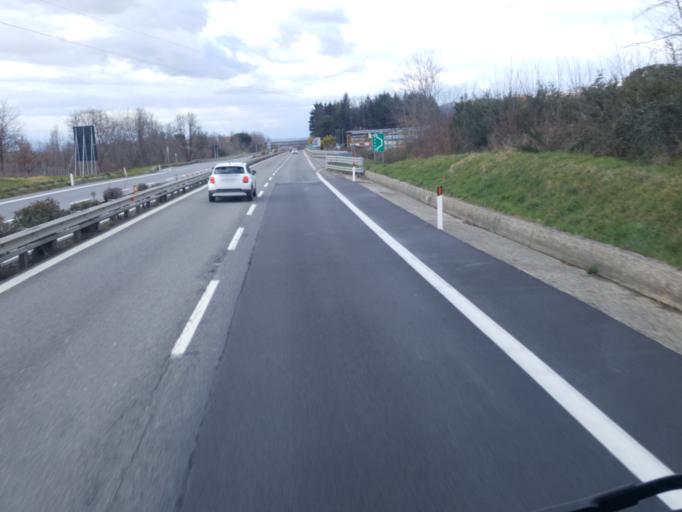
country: IT
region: Calabria
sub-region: Provincia di Cosenza
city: Piane Crati
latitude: 39.2183
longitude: 16.3051
